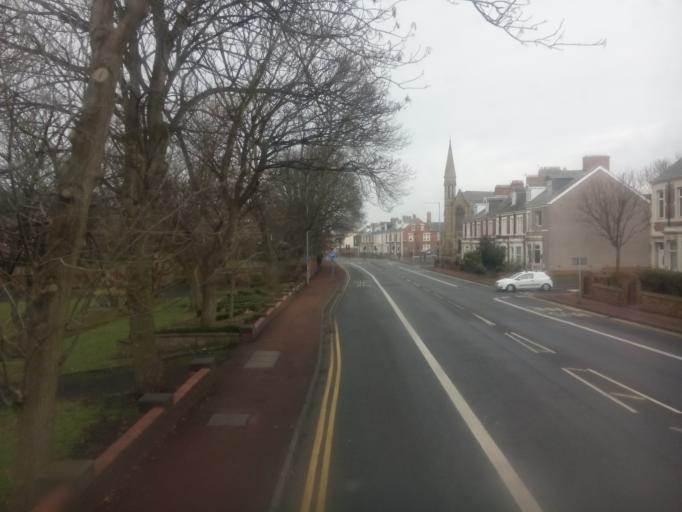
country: GB
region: England
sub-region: Gateshead
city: Gateshead
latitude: 54.9501
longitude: -1.5992
